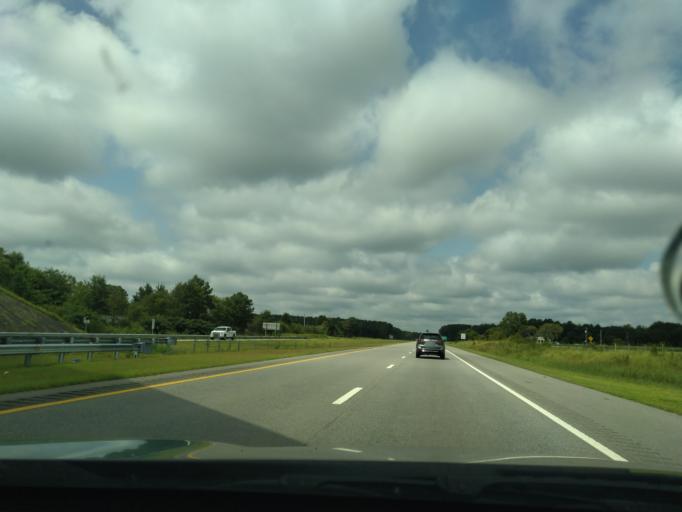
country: US
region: North Carolina
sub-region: Martin County
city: Williamston
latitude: 35.8181
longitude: -77.0799
